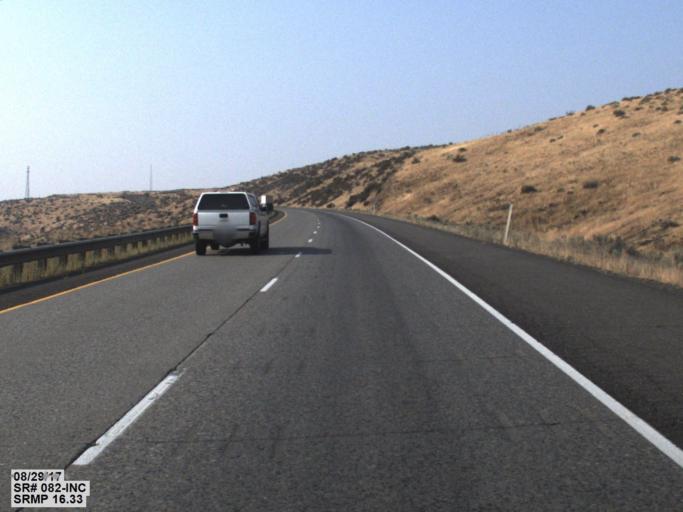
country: US
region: Washington
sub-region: Yakima County
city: Terrace Heights
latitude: 46.7852
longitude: -120.3698
